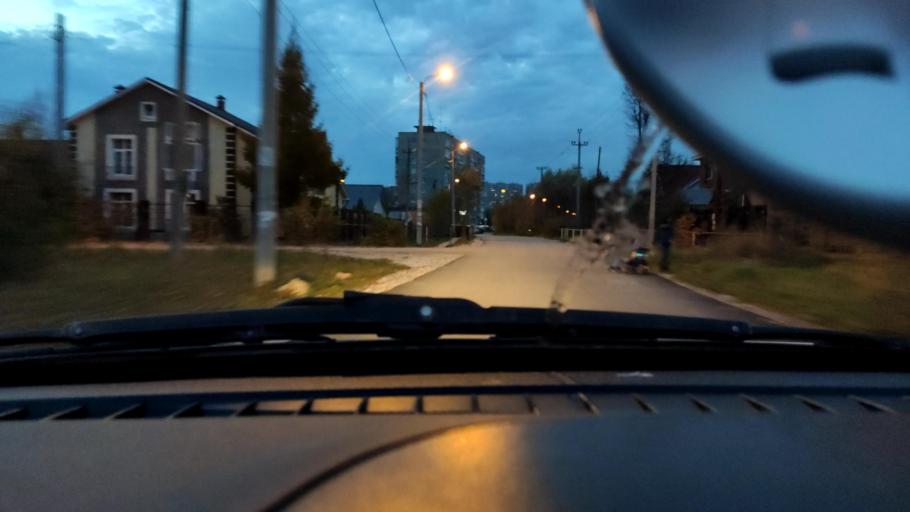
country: RU
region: Perm
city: Perm
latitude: 57.9768
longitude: 56.2985
